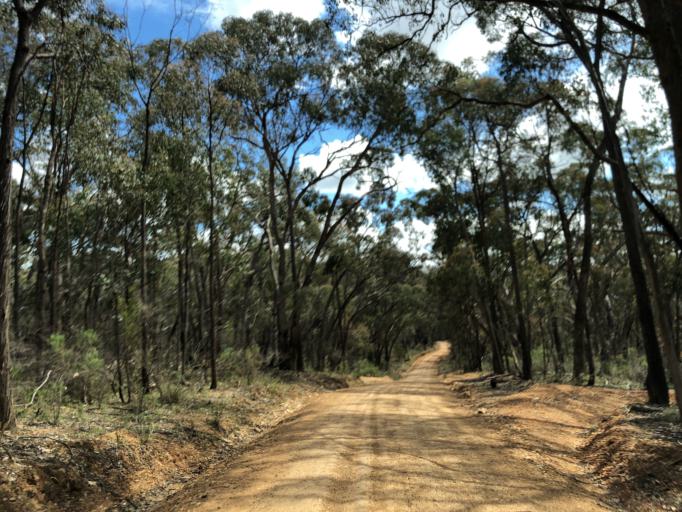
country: AU
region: Victoria
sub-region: Benalla
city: Benalla
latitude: -36.7519
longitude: 146.1638
